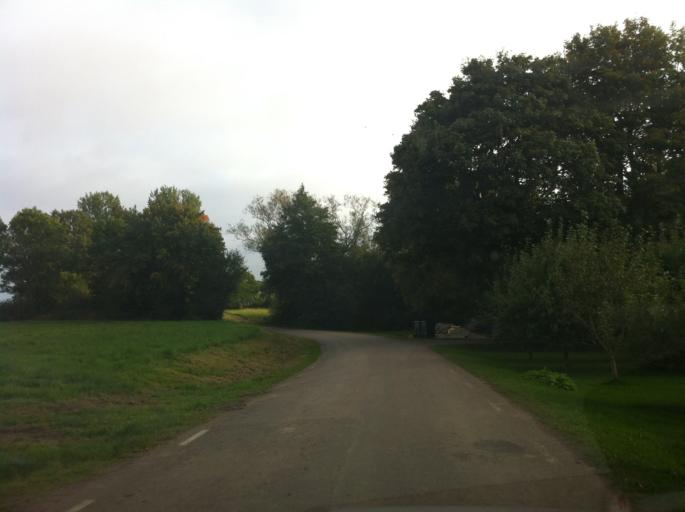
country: SE
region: Skane
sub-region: Helsingborg
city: Barslov
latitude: 55.9759
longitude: 12.8832
